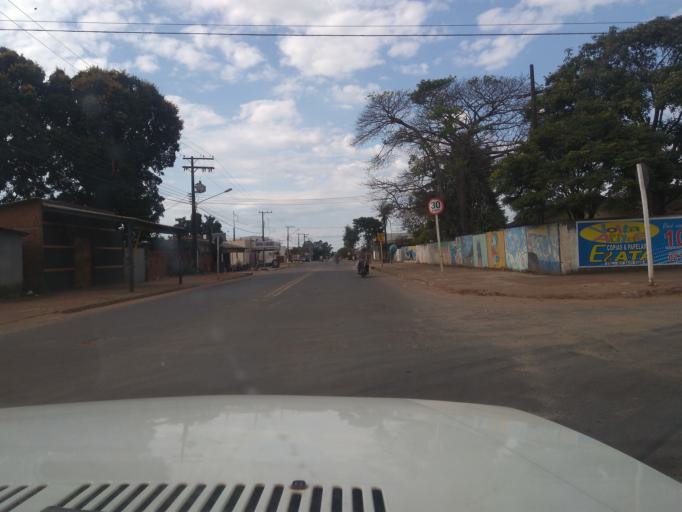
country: BR
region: Mato Grosso do Sul
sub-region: Ponta Pora
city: Ponta Pora
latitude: -22.5618
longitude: -55.6941
